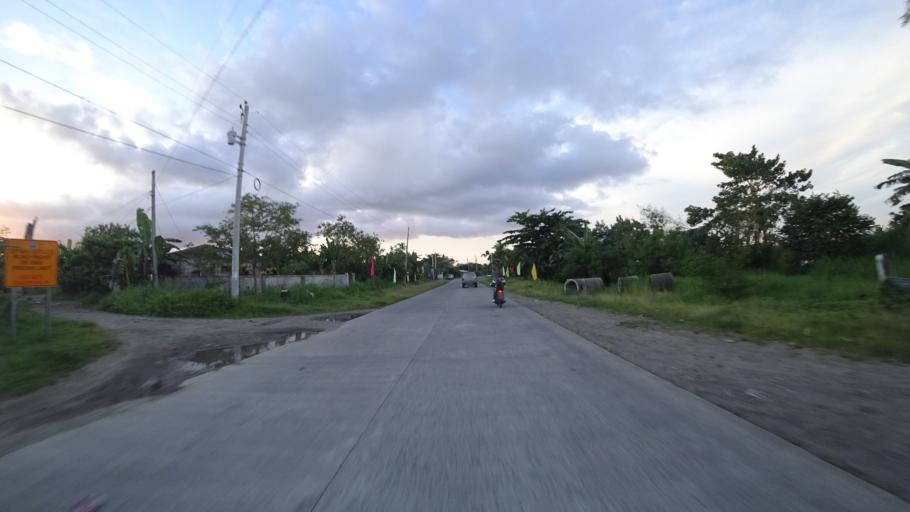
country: PH
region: Eastern Visayas
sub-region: Province of Leyte
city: Palo
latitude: 11.1556
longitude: 125.0015
